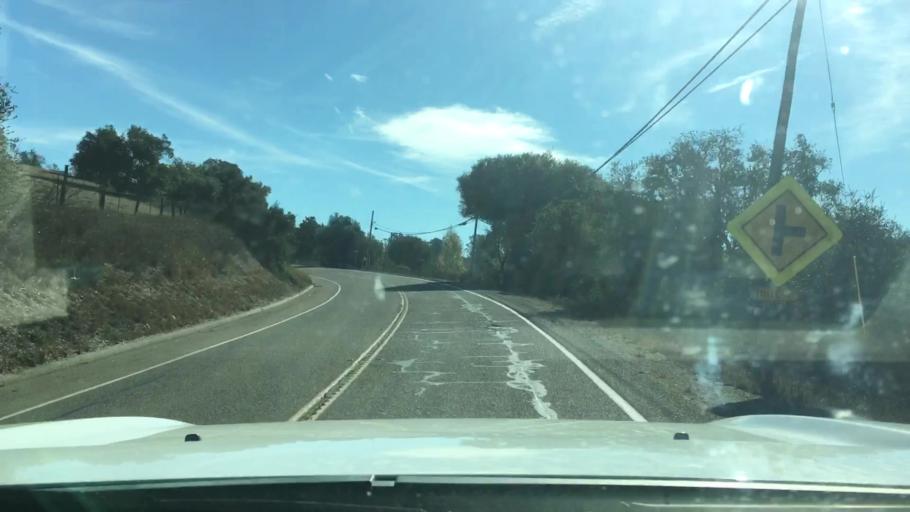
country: US
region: California
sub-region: San Luis Obispo County
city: Nipomo
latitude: 35.0737
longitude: -120.5224
